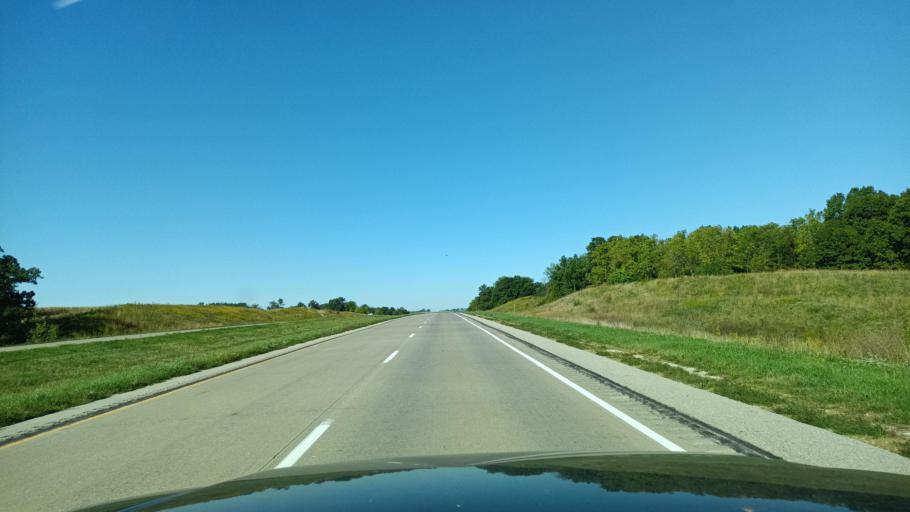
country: US
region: Iowa
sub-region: Lee County
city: Fort Madison
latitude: 40.6707
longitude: -91.3044
